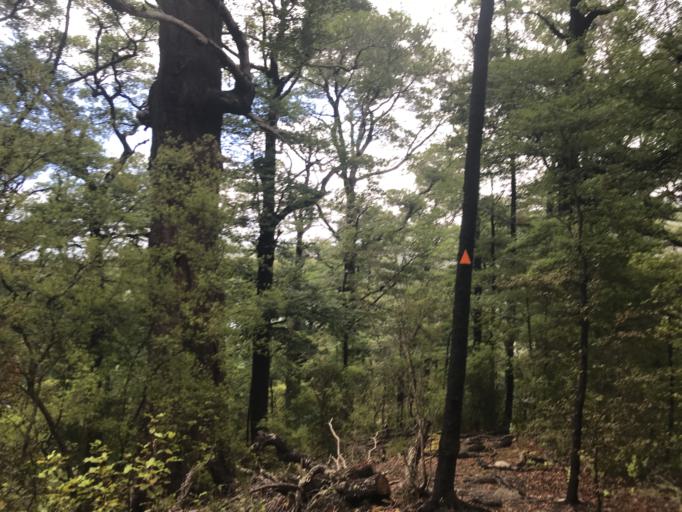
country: NZ
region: Marlborough
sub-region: Marlborough District
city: Picton
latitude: -41.2195
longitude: 173.9753
